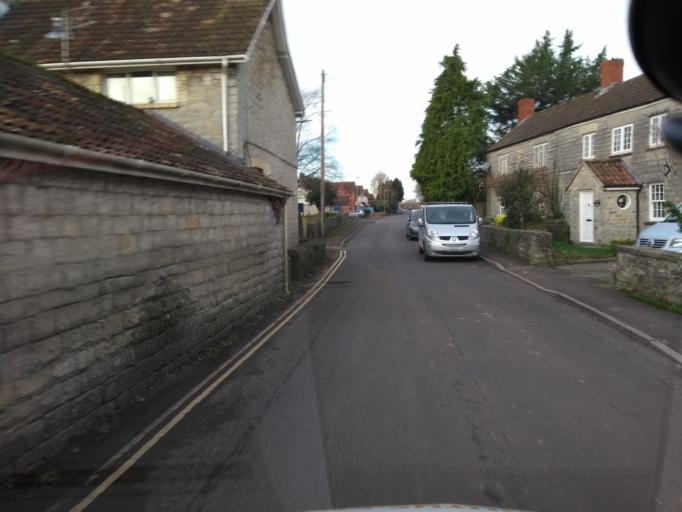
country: GB
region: England
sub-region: Somerset
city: Street
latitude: 51.1206
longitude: -2.7334
